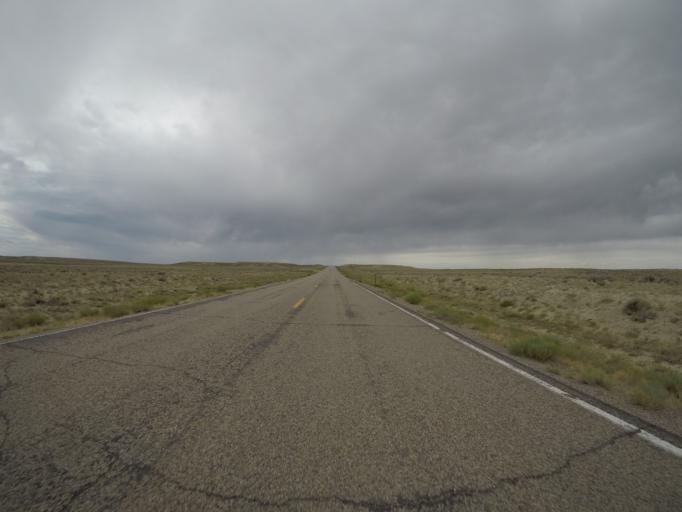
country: US
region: Wyoming
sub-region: Lincoln County
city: Kemmerer
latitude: 41.9637
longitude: -110.1469
